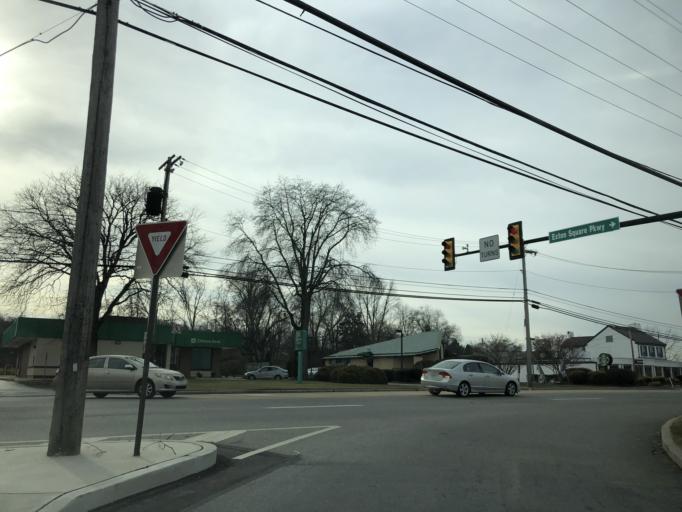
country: US
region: Pennsylvania
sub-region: Chester County
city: Exton
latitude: 40.0290
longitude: -75.6216
